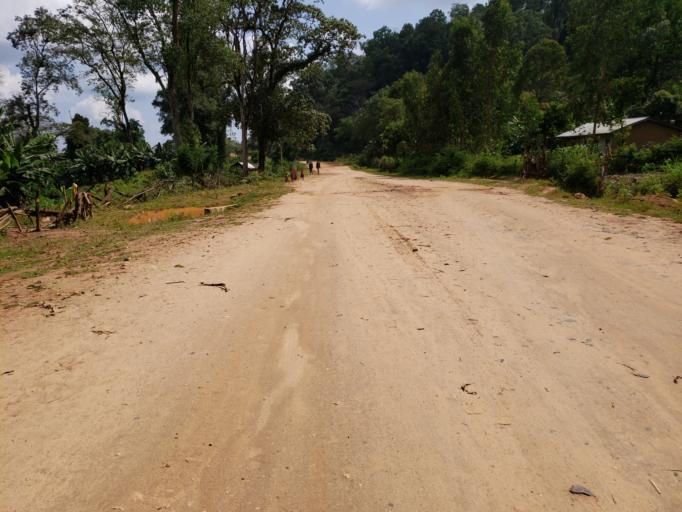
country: ET
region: Oromiya
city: Dodola
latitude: 6.4518
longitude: 39.5698
